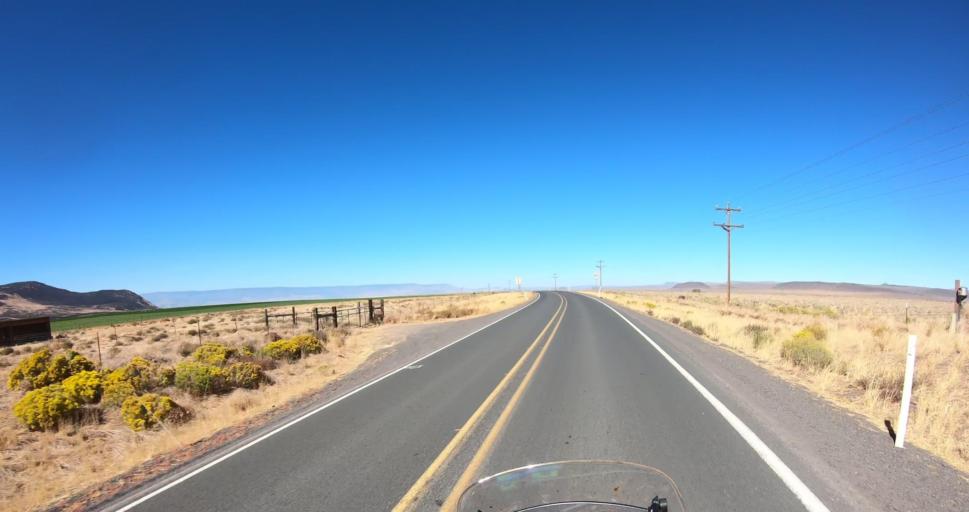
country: US
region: Oregon
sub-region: Lake County
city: Lakeview
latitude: 42.7018
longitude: -120.5469
